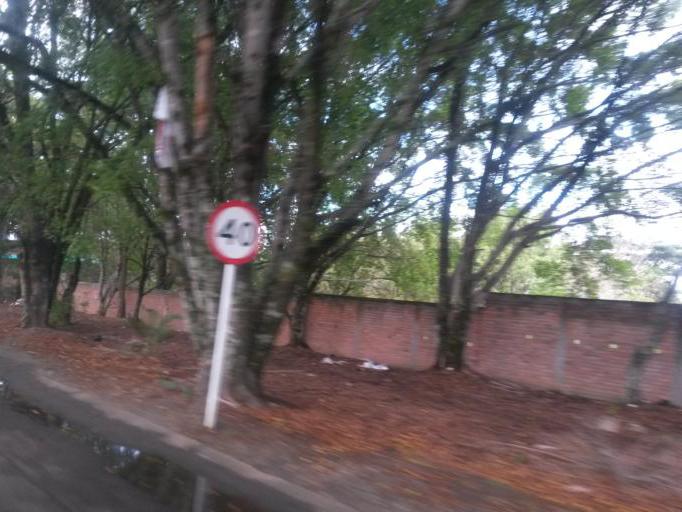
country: CO
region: Cauca
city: El Bordo
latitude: 2.1264
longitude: -76.9750
